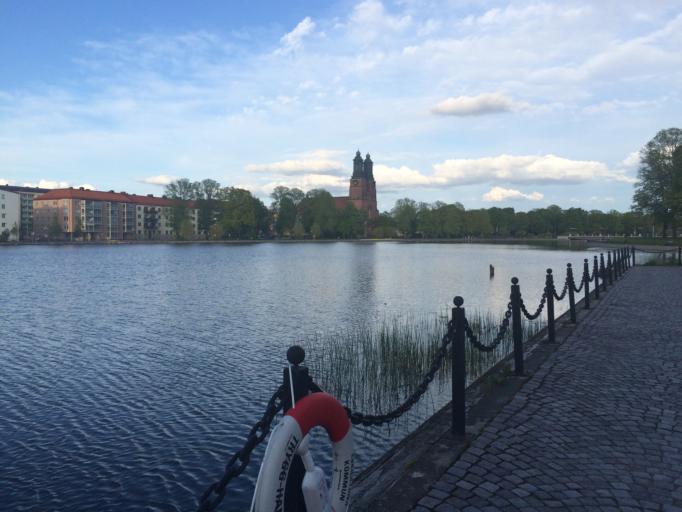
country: SE
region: Soedermanland
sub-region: Eskilstuna Kommun
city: Eskilstuna
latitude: 59.3751
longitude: 16.5107
